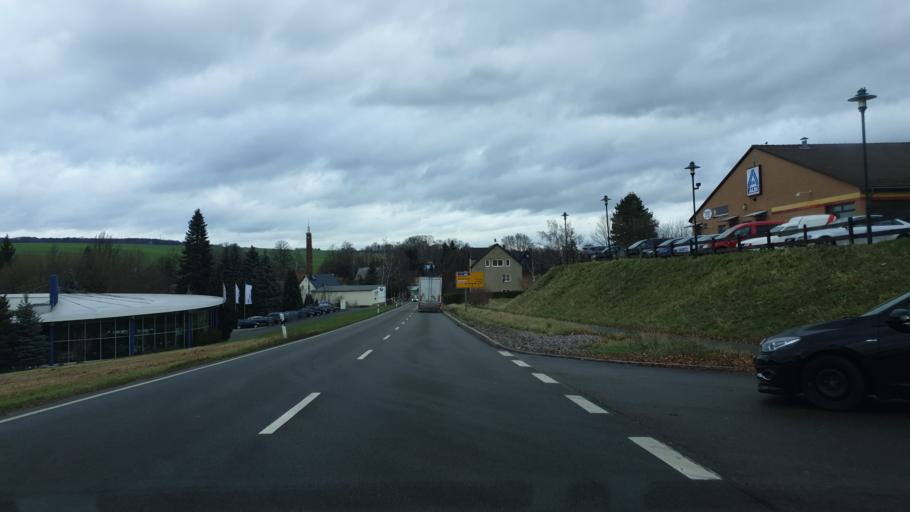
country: DE
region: Saxony
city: Oberlungwitz
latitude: 50.7799
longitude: 12.6949
